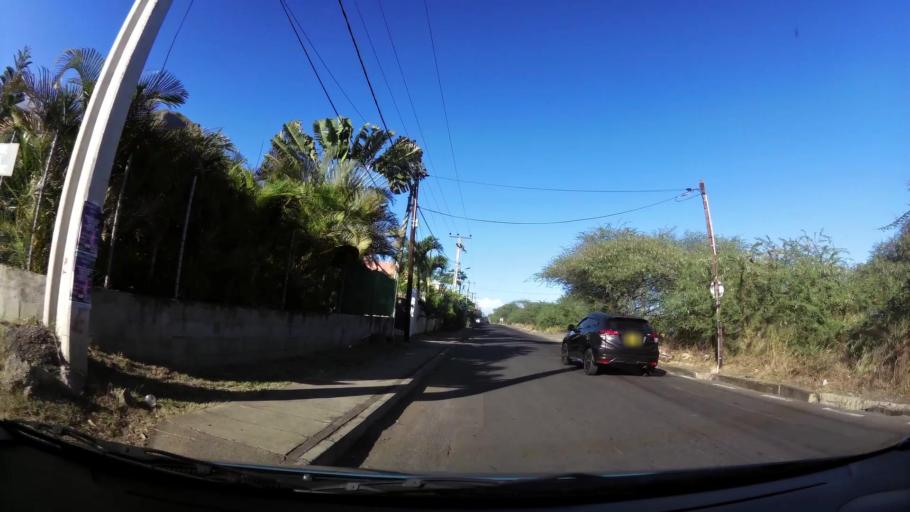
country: MU
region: Black River
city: Tamarin
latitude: -20.3362
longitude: 57.3707
